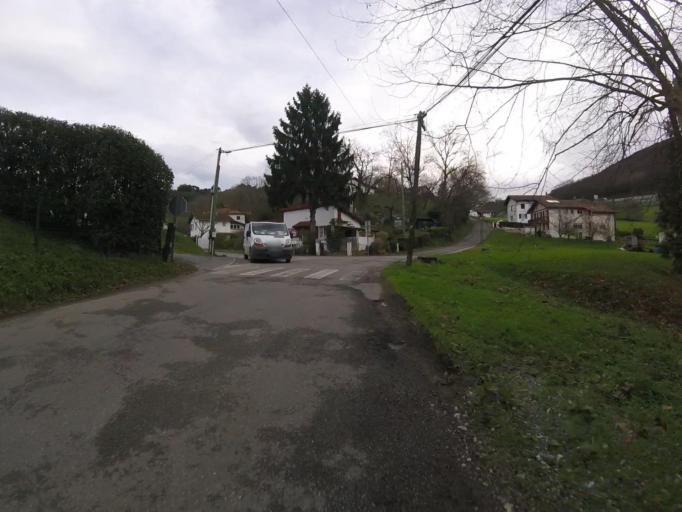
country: FR
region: Aquitaine
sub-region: Departement des Pyrenees-Atlantiques
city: Hendaye
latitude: 43.3426
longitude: -1.7395
